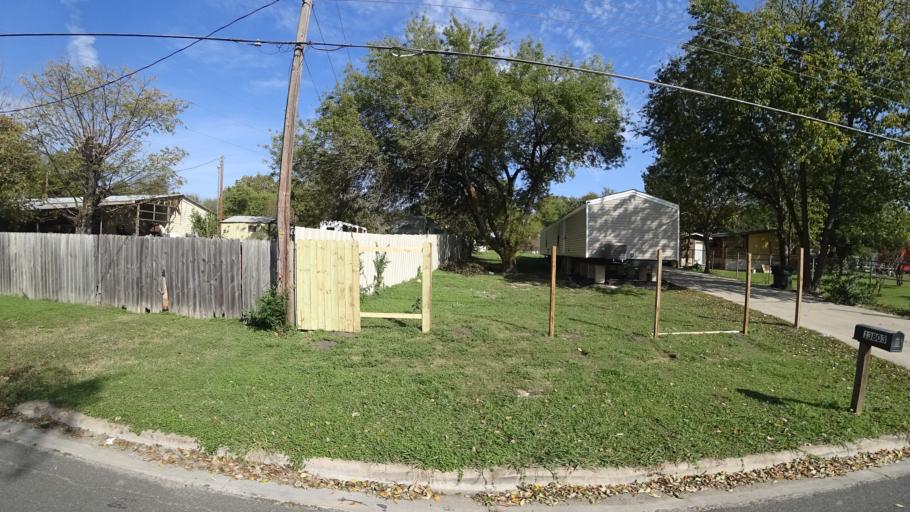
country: US
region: Texas
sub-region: Travis County
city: Pflugerville
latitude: 30.4076
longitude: -97.6342
